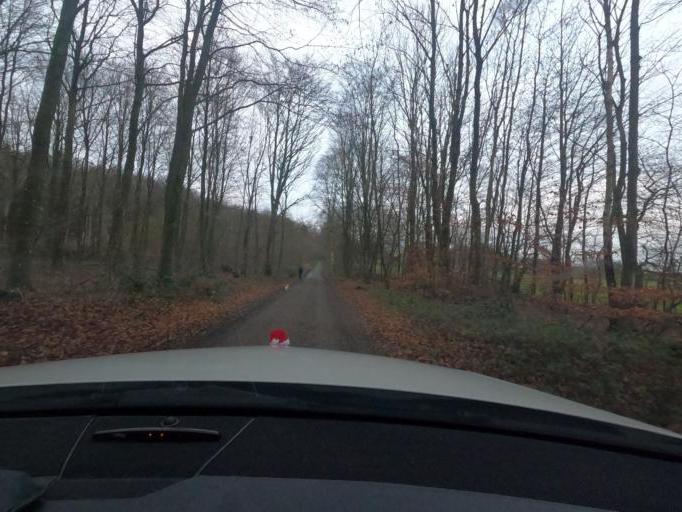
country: DK
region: South Denmark
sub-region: Sonderborg Kommune
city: Sonderborg
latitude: 54.8958
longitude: 9.8515
